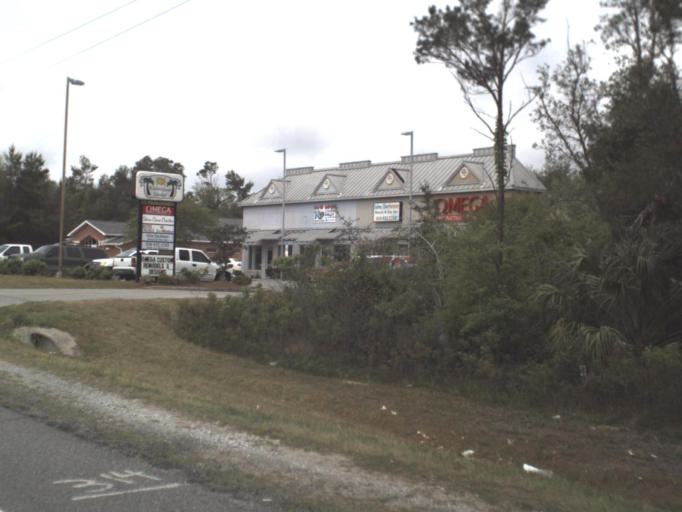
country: US
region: Florida
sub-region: Santa Rosa County
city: Oriole Beach
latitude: 30.3843
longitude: -87.1041
